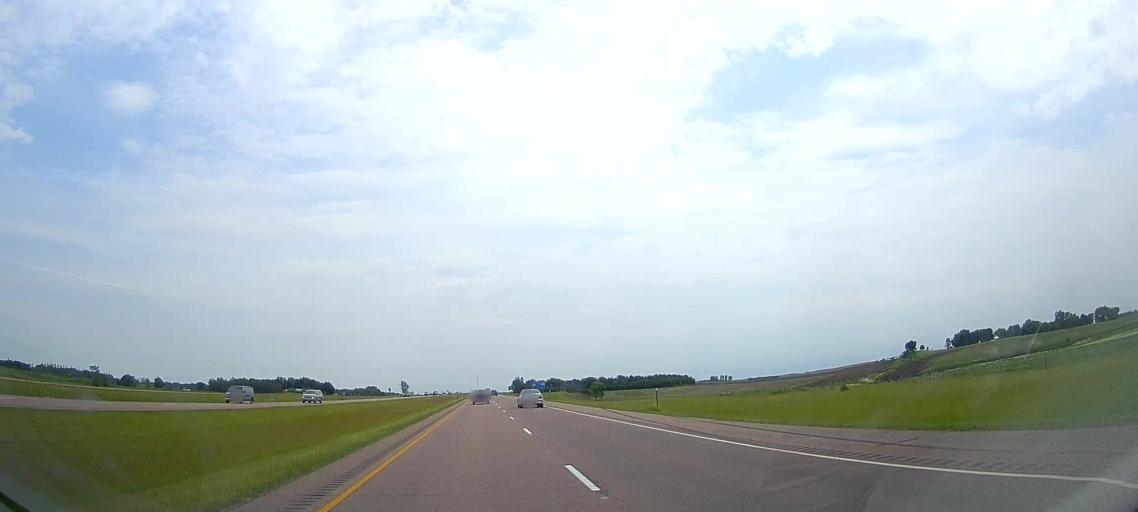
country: US
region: South Dakota
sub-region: Minnehaha County
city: Hartford
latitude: 43.6512
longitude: -97.0993
